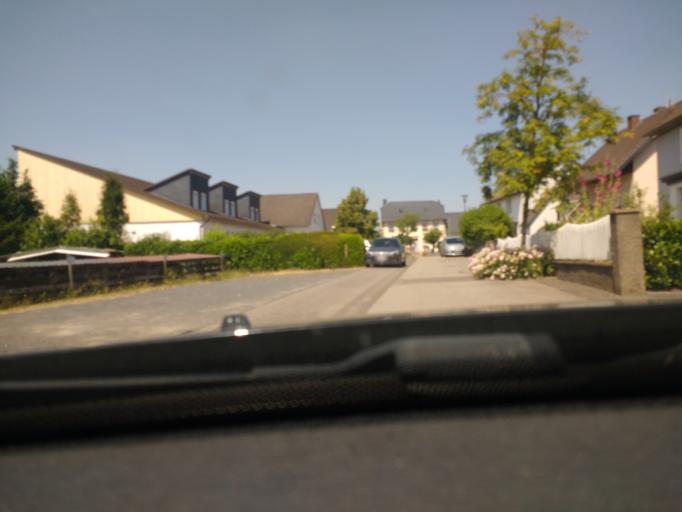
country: DE
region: Rheinland-Pfalz
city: Laufeld
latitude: 50.0792
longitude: 6.8683
